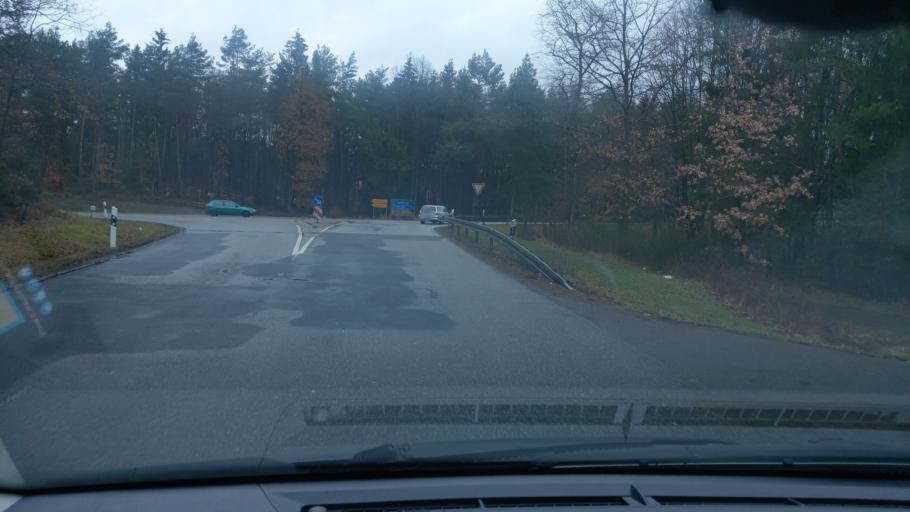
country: DE
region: Rheinland-Pfalz
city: Bechhofen
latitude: 49.3599
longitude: 7.3845
